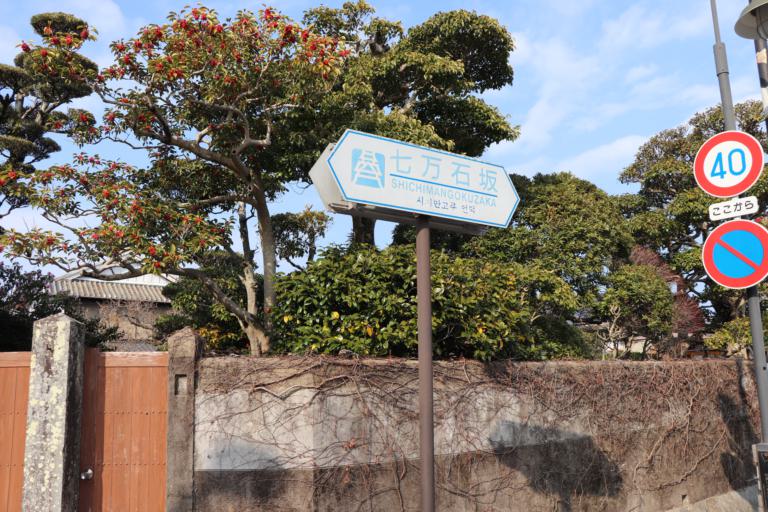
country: JP
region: Nagasaki
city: Shimabara
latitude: 32.7897
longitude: 130.3684
